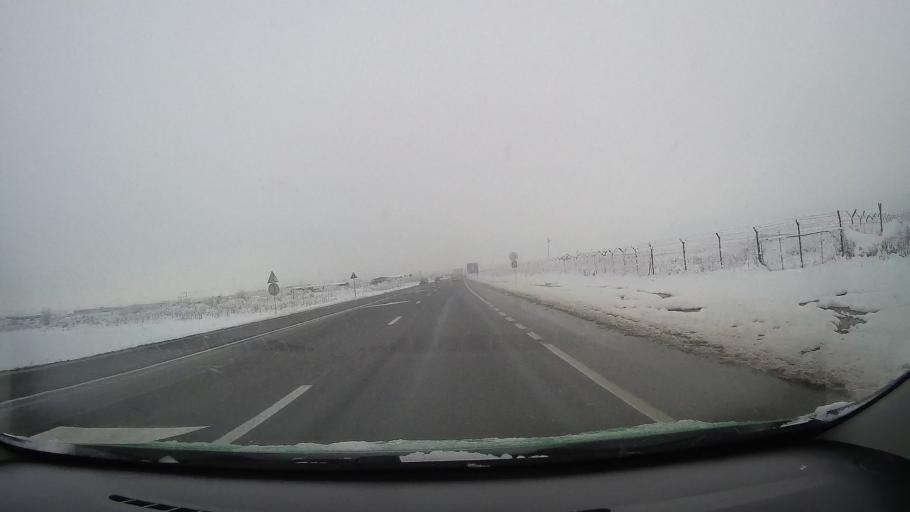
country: RO
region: Sibiu
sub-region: Comuna Cristian
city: Cristian
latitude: 45.7889
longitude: 24.0644
